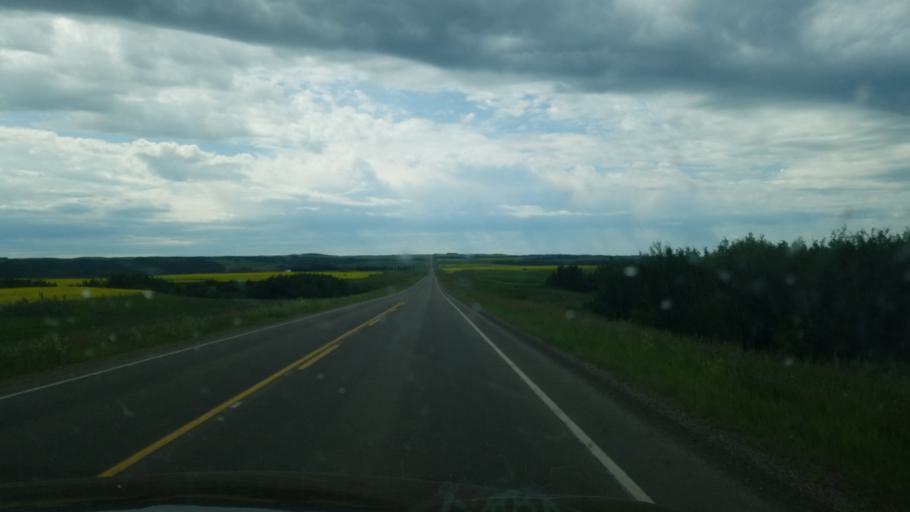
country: CA
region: Saskatchewan
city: Unity
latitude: 52.9193
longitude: -109.3425
